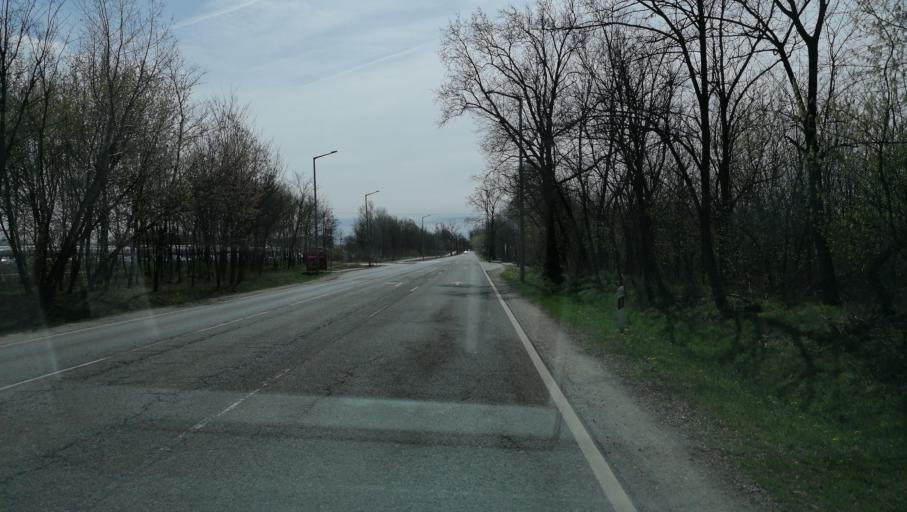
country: HU
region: Pest
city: Alsonemedi
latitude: 47.3454
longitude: 19.1567
